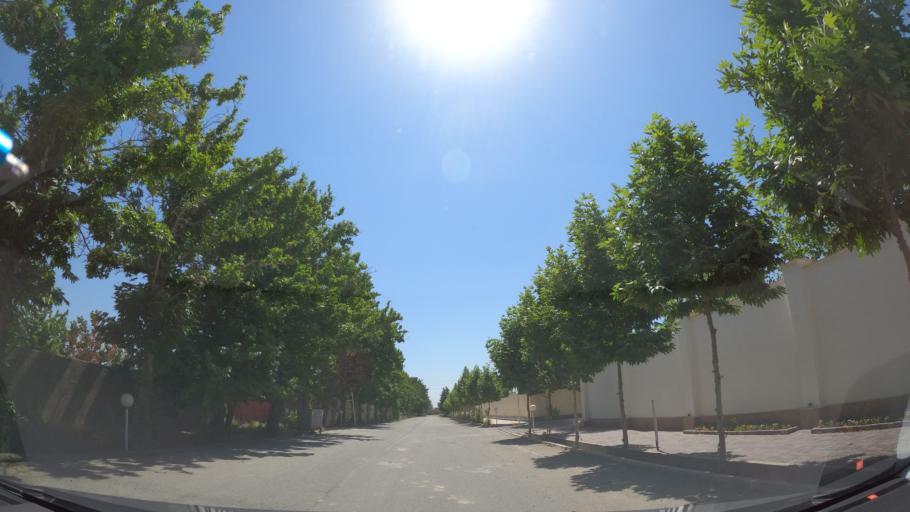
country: IR
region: Alborz
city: Hashtgerd
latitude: 35.9139
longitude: 50.7208
